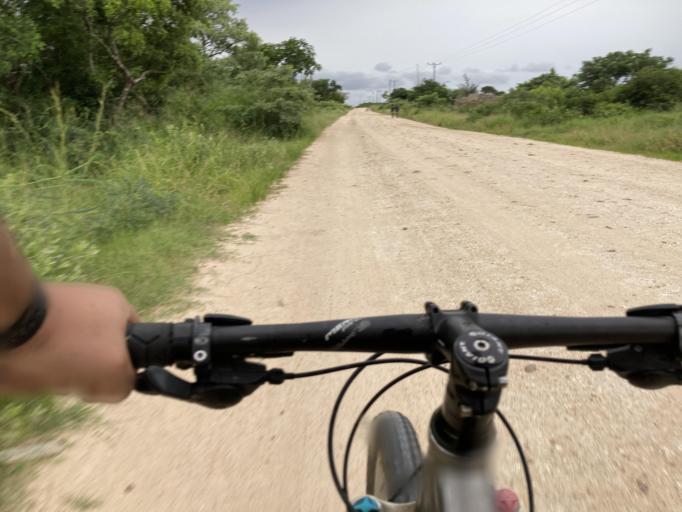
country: MZ
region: Maputo City
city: Maputo
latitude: -26.0492
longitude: 32.5339
